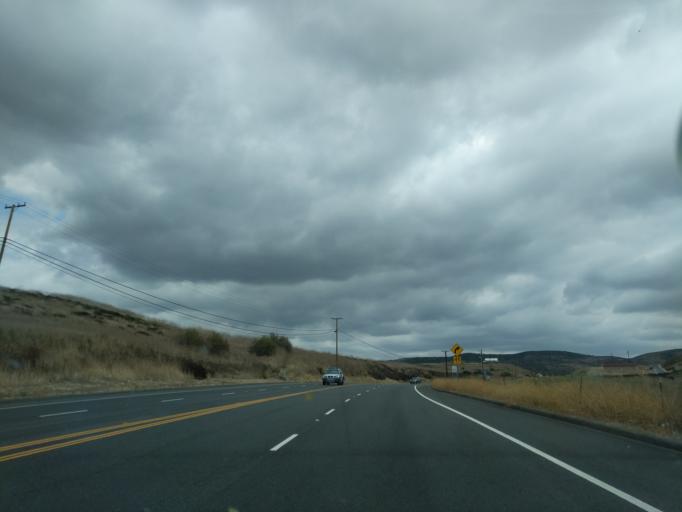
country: US
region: California
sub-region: Orange County
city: North Tustin
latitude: 33.7914
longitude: -117.7586
